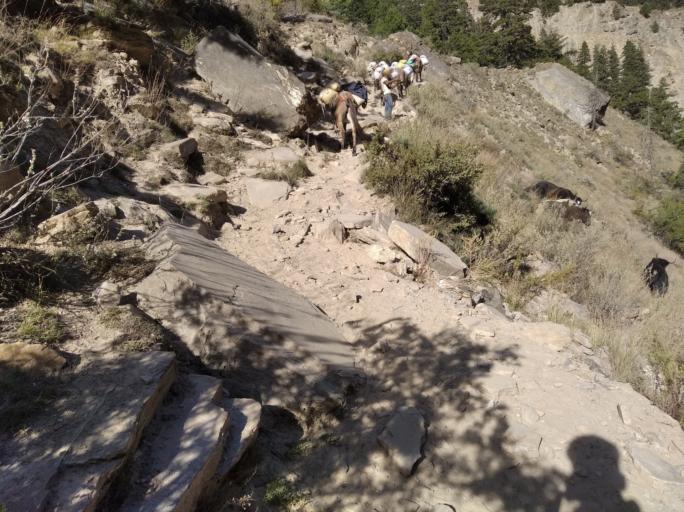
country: NP
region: Western Region
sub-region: Dhawalagiri Zone
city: Jomsom
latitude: 28.8764
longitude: 83.1445
